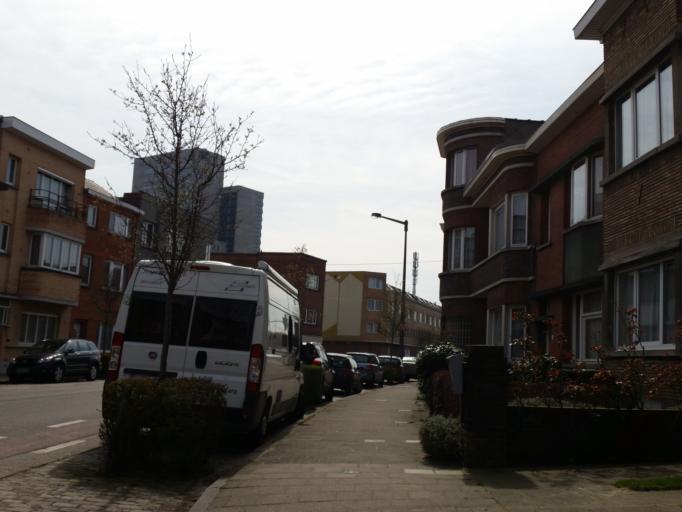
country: BE
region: Flanders
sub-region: Provincie Oost-Vlaanderen
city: Gent
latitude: 51.0395
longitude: 3.7058
